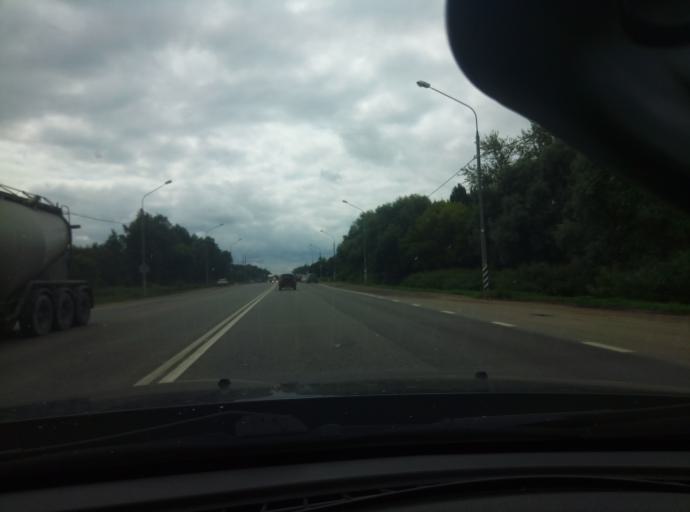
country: RU
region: Kaluga
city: Obninsk
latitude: 55.0913
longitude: 36.6349
